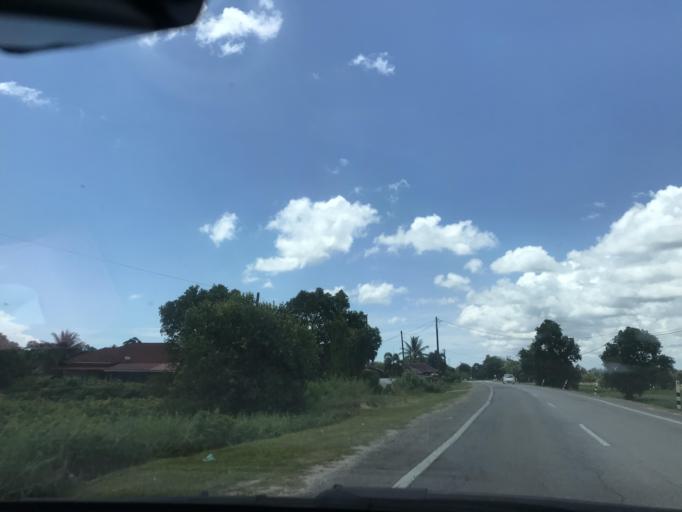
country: MY
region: Kelantan
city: Tumpat
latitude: 6.2085
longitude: 102.1113
